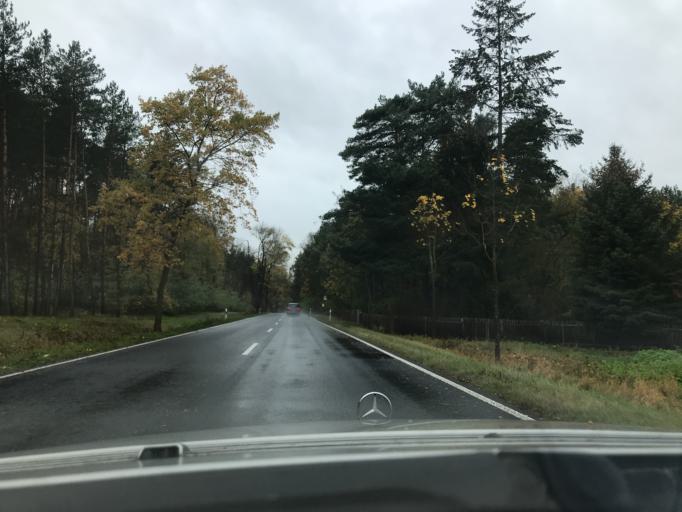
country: DE
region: Brandenburg
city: Trebbin
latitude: 52.2233
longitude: 13.1896
